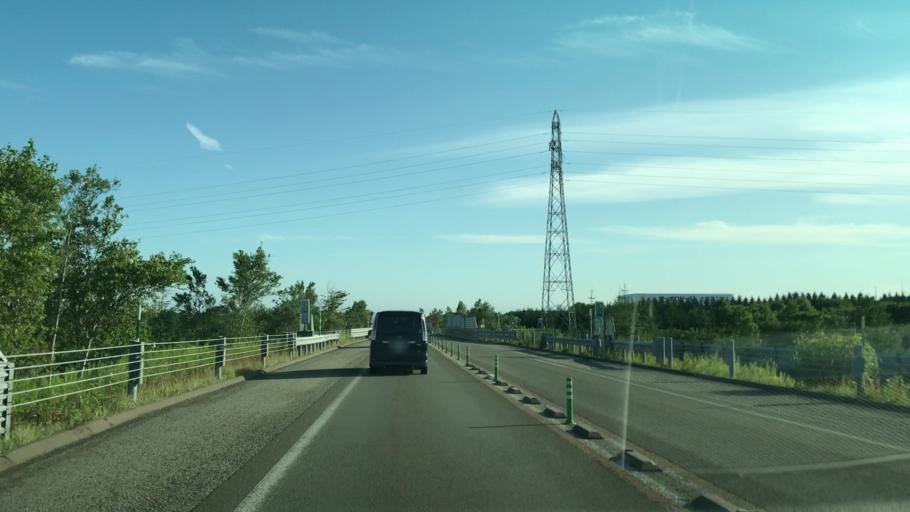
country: JP
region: Hokkaido
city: Chitose
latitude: 42.8652
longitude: 141.6094
